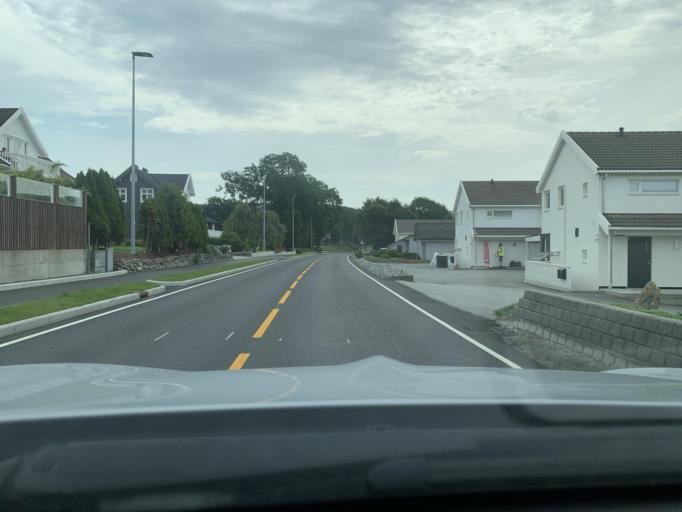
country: NO
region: Rogaland
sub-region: Sandnes
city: Sandnes
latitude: 58.7759
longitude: 5.7218
